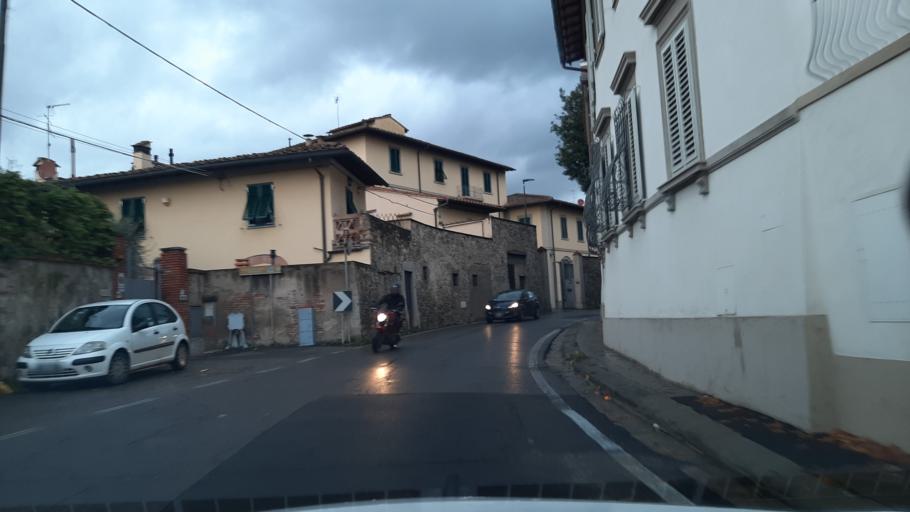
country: IT
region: Tuscany
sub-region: Province of Florence
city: Florence
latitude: 43.7950
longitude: 11.2611
